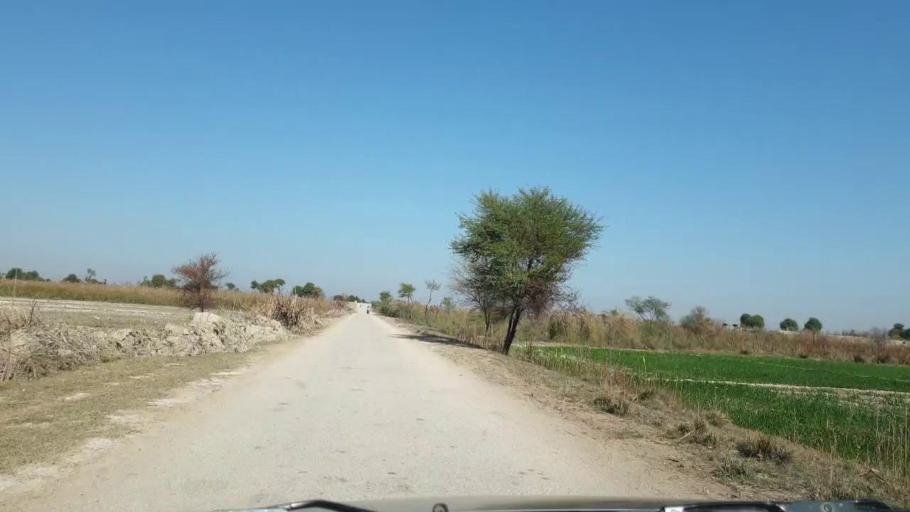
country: PK
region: Sindh
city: Sinjhoro
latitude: 26.1034
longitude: 68.8428
